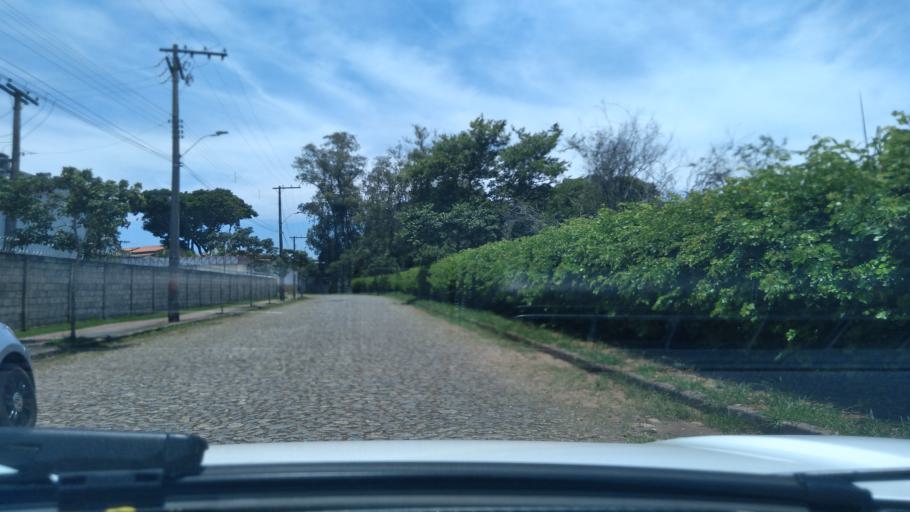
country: BR
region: Minas Gerais
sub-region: Contagem
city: Contagem
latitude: -19.9311
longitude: -44.0108
